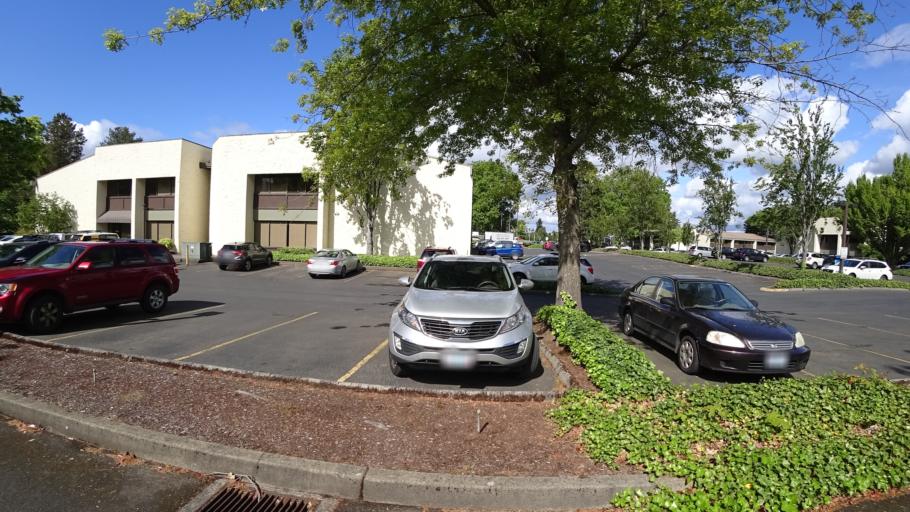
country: US
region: Oregon
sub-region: Washington County
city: Metzger
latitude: 45.4265
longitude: -122.7490
